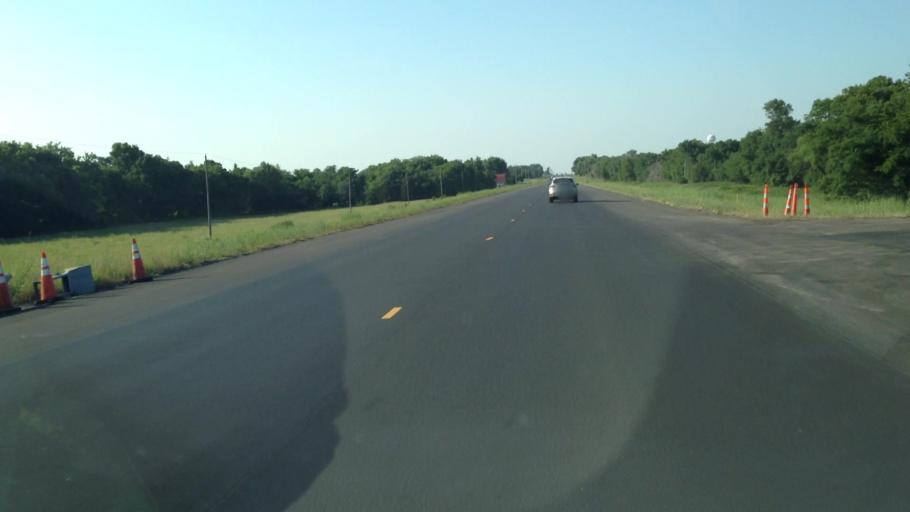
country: US
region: Kansas
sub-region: Franklin County
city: Ottawa
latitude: 38.4776
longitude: -95.2673
